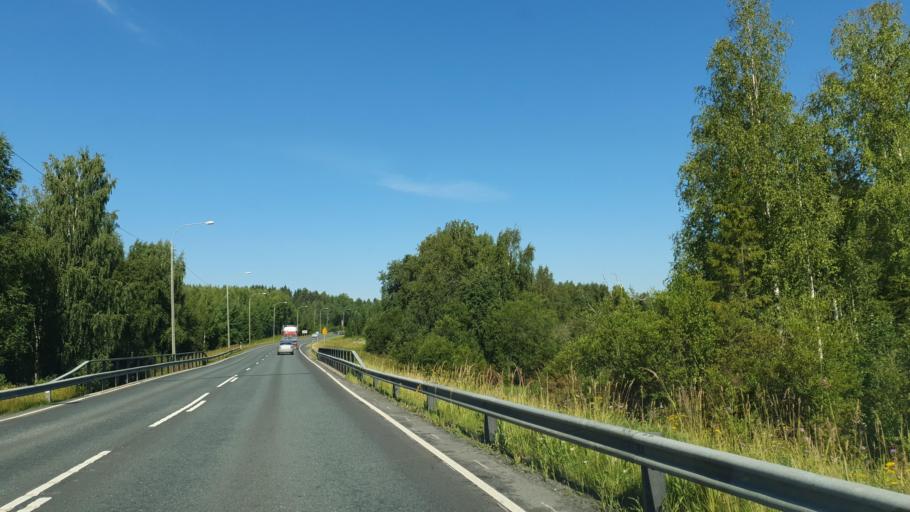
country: FI
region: Northern Savo
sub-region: Ylae-Savo
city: Lapinlahti
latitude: 63.2192
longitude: 27.5156
